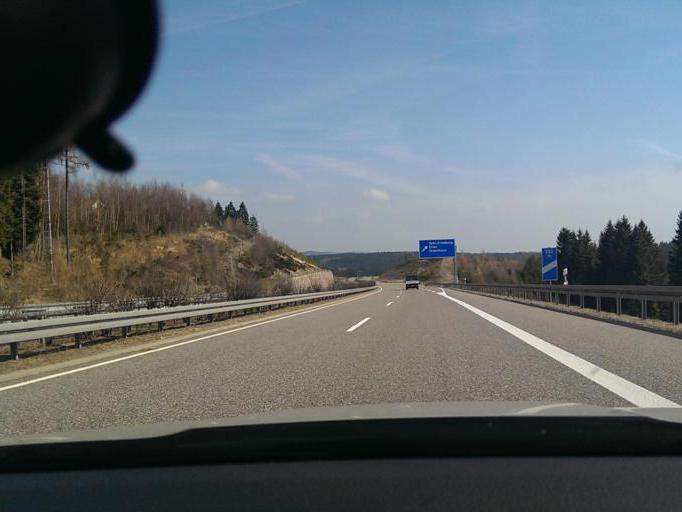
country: DE
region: Thuringia
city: Suhl
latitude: 50.5779
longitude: 10.7159
